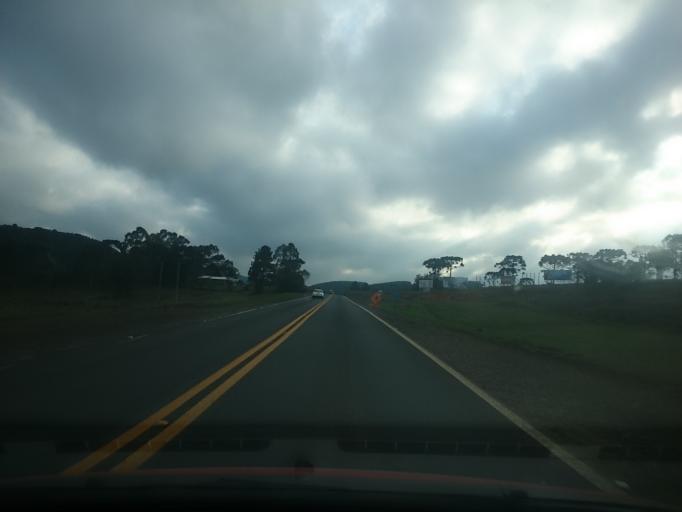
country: BR
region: Santa Catarina
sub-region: Lages
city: Lages
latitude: -27.9521
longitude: -50.4796
